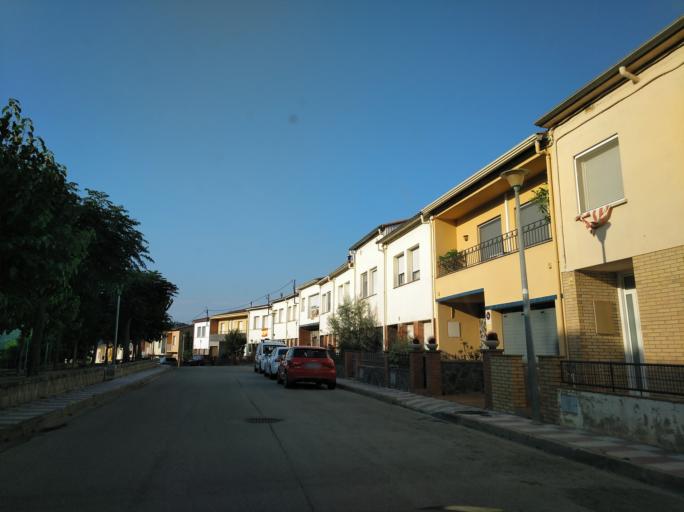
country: ES
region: Catalonia
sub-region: Provincia de Girona
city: Angles
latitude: 41.9508
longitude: 2.6366
